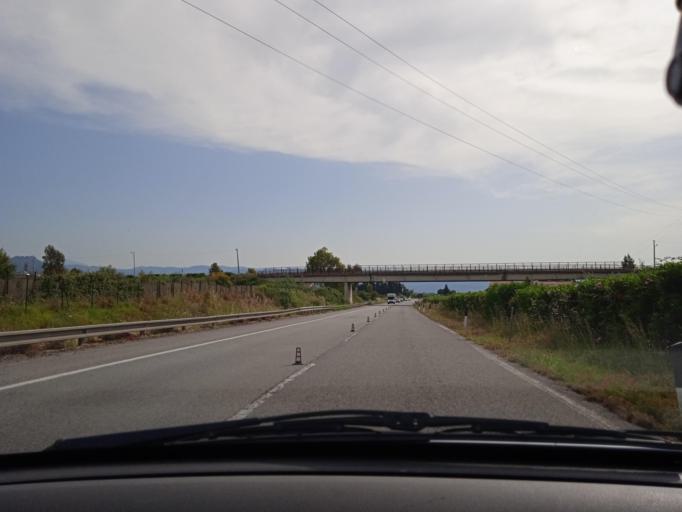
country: IT
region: Sicily
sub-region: Messina
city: Terme
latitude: 38.1458
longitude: 15.1690
